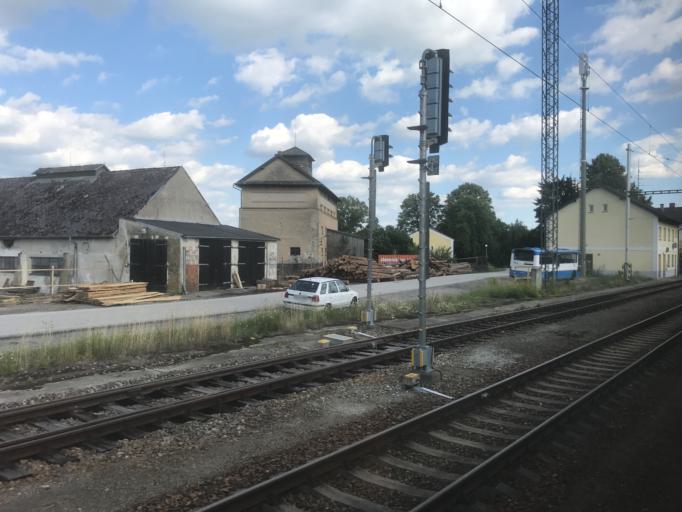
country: CZ
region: Jihocesky
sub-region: Okres Cesky Krumlov
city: Dolni Dvoriste
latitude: 48.6504
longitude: 14.4317
